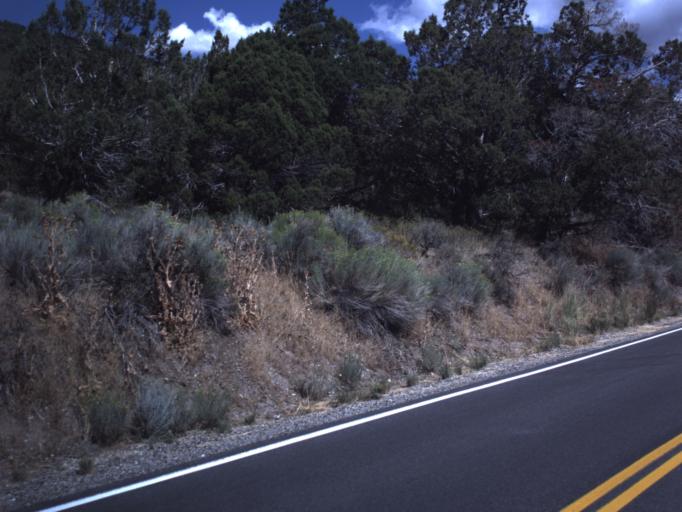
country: US
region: Utah
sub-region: Tooele County
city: Grantsville
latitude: 40.3454
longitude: -112.5867
